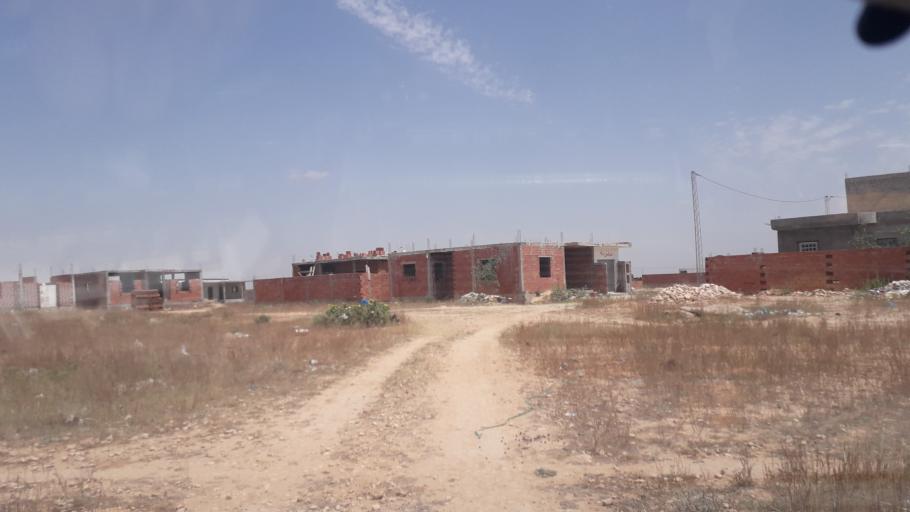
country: TN
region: Safaqis
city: Al Qarmadah
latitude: 34.8457
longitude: 10.7736
